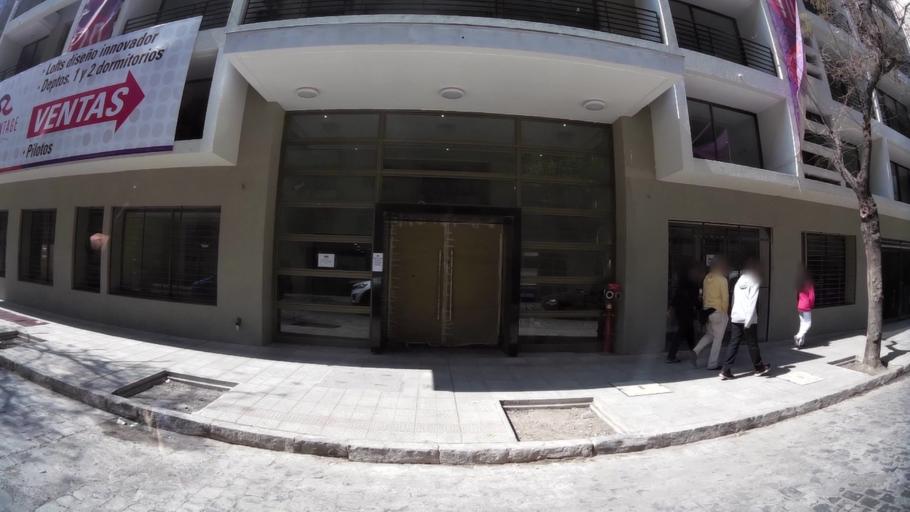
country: CL
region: Santiago Metropolitan
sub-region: Provincia de Santiago
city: Santiago
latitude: -33.4539
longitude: -70.6613
